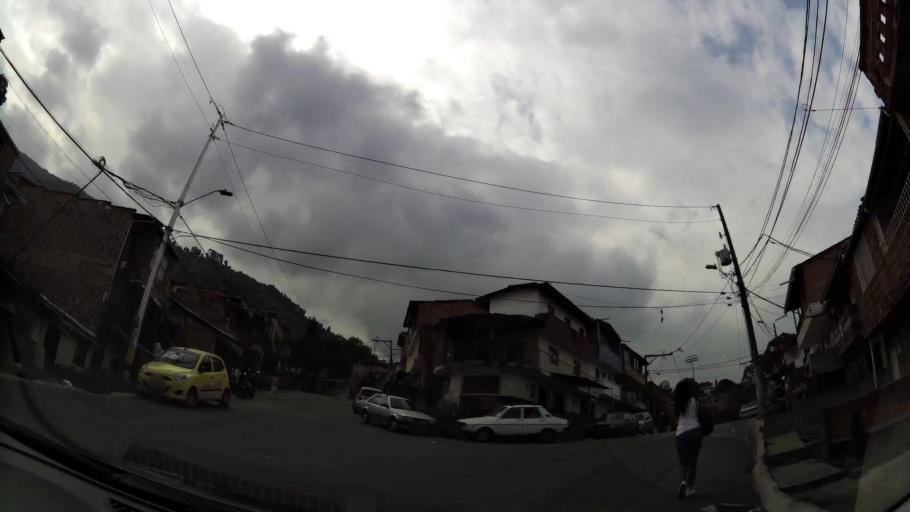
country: CO
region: Antioquia
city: Medellin
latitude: 6.2825
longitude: -75.5484
